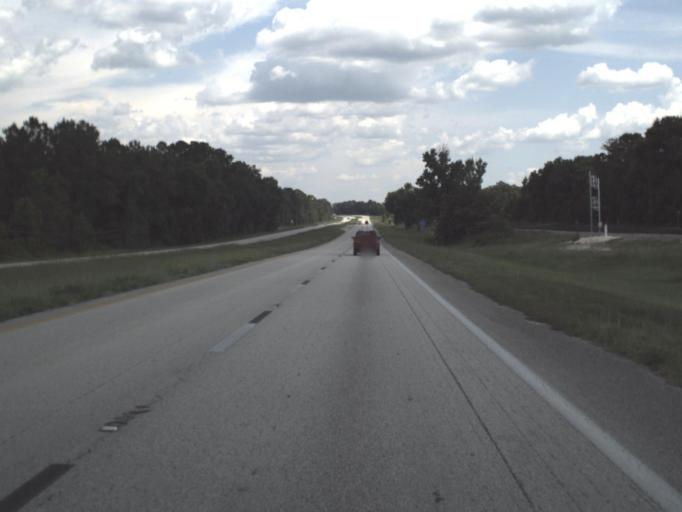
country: US
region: Florida
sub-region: Alachua County
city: Hawthorne
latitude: 29.6253
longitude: -82.0995
